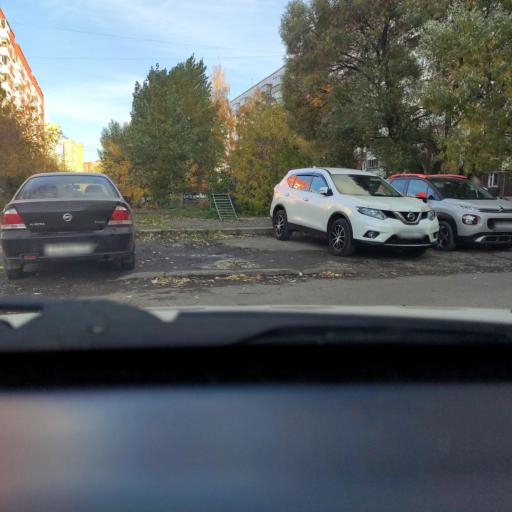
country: RU
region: Perm
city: Kondratovo
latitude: 57.9982
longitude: 56.1423
